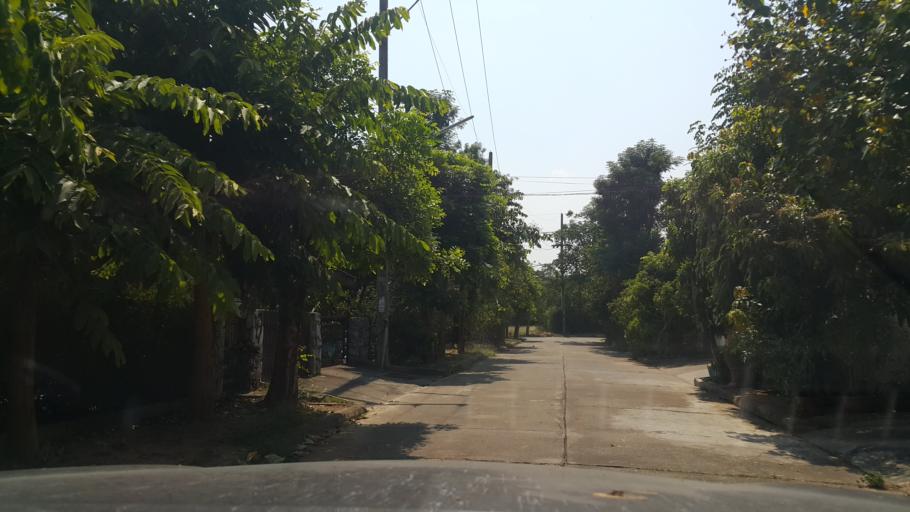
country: TH
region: Chiang Mai
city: Chiang Mai
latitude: 18.7285
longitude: 98.9694
